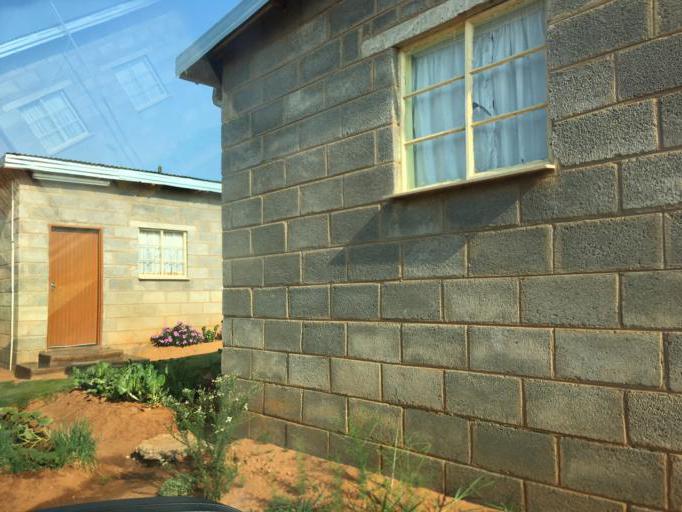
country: LS
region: Maseru
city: Maseru
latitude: -29.4291
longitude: 27.5678
